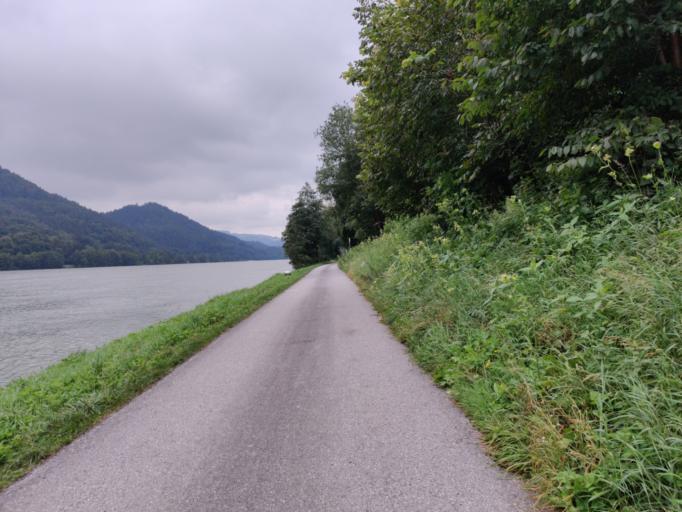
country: AT
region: Lower Austria
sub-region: Politischer Bezirk Melk
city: Nochling
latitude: 48.2231
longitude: 14.9450
